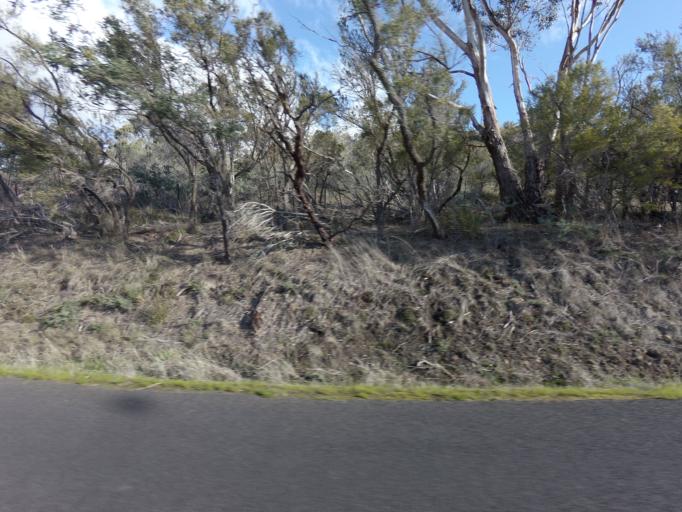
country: AU
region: Tasmania
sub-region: Derwent Valley
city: New Norfolk
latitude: -42.7461
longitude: 147.0420
